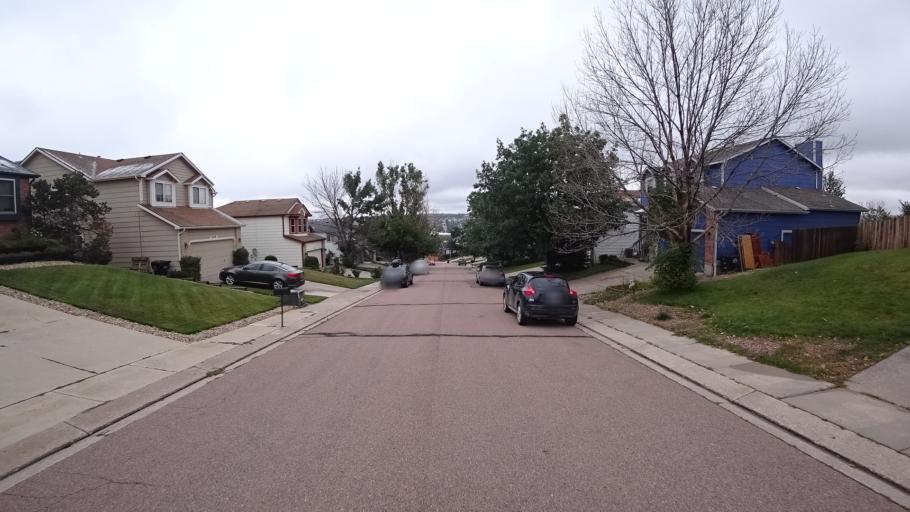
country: US
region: Colorado
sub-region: El Paso County
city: Cimarron Hills
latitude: 38.9231
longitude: -104.7571
